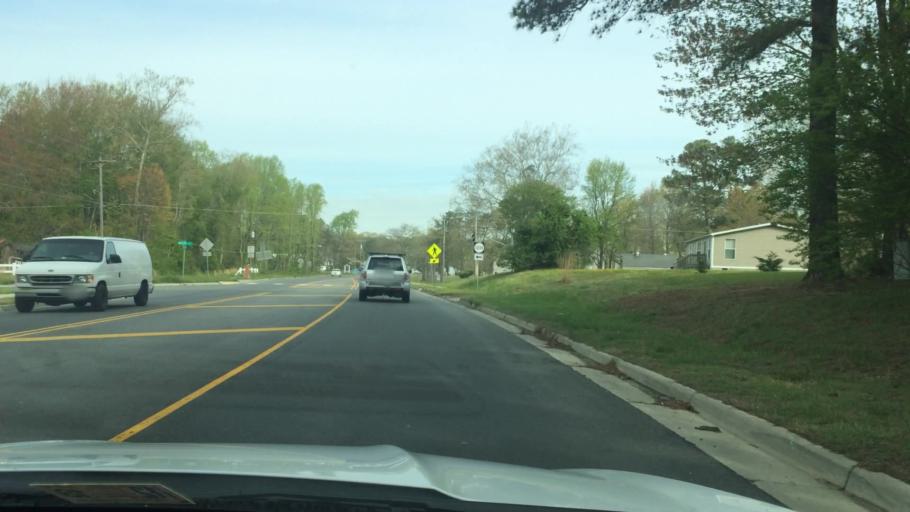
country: US
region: Virginia
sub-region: Lancaster County
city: Kilmarnock
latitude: 37.7010
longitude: -76.3751
